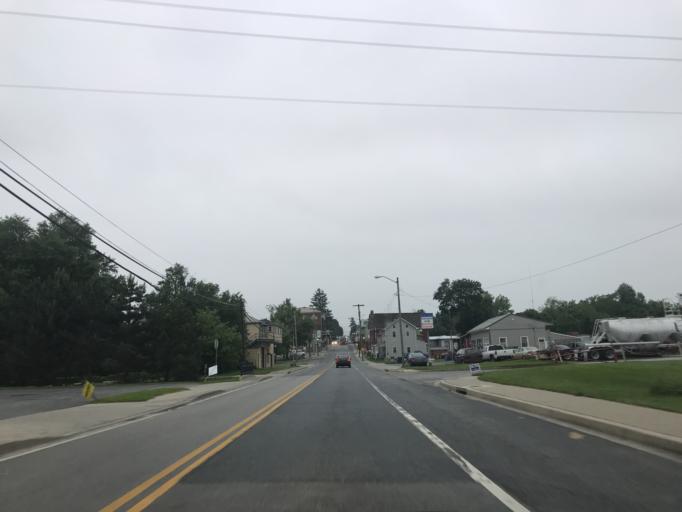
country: US
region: Maryland
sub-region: Carroll County
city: New Windsor
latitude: 39.5721
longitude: -77.1764
